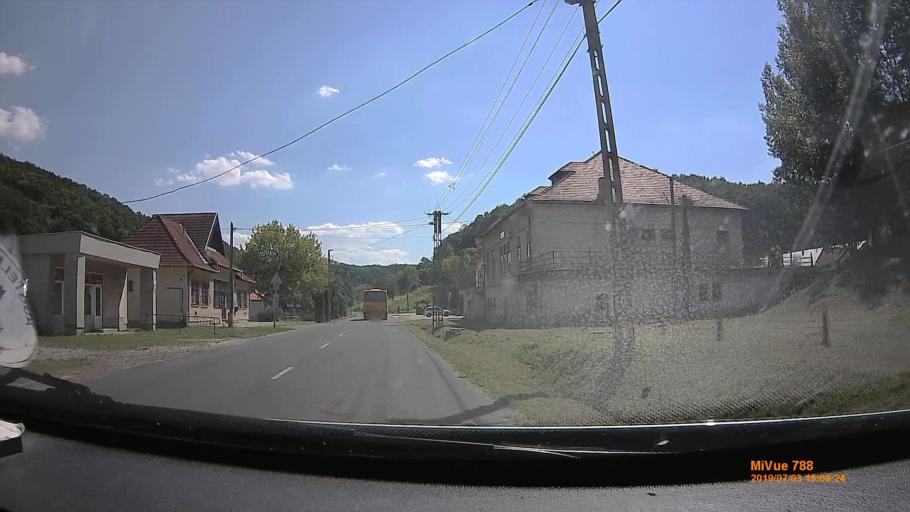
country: HU
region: Borsod-Abauj-Zemplen
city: Ozd
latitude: 48.2377
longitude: 20.3735
